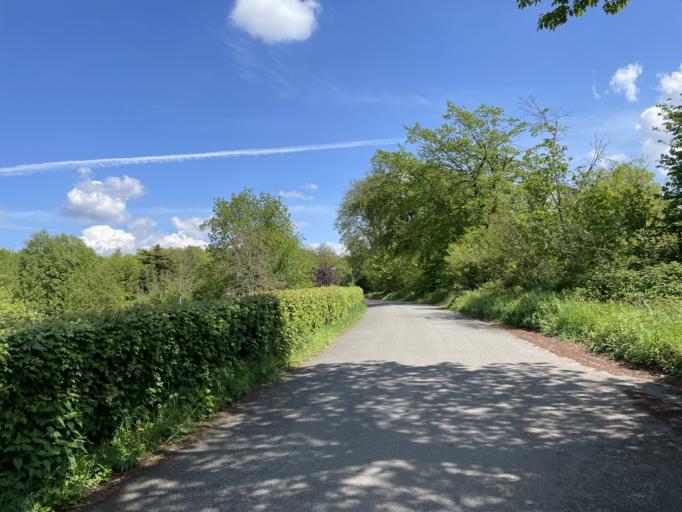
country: DE
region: North Rhine-Westphalia
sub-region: Regierungsbezirk Dusseldorf
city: Heiligenhaus
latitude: 51.3685
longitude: 6.9550
